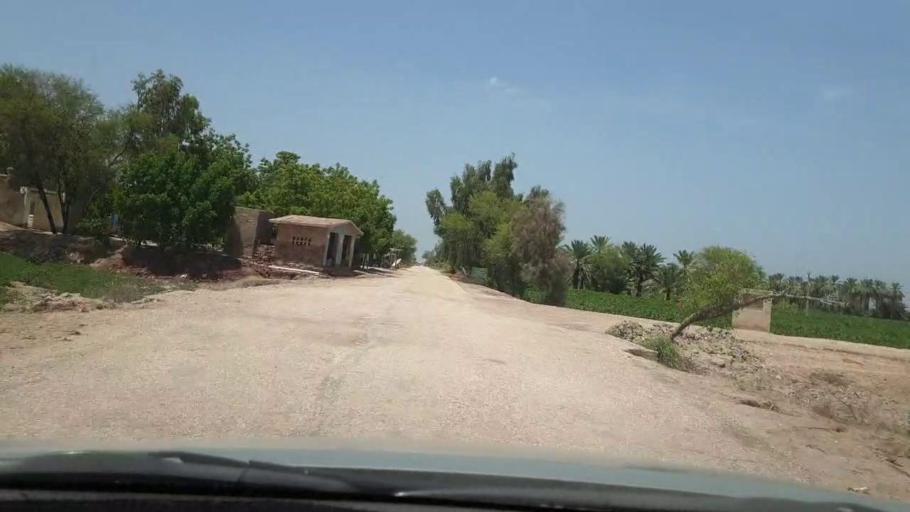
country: PK
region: Sindh
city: Pano Aqil
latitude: 27.7083
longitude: 69.2166
